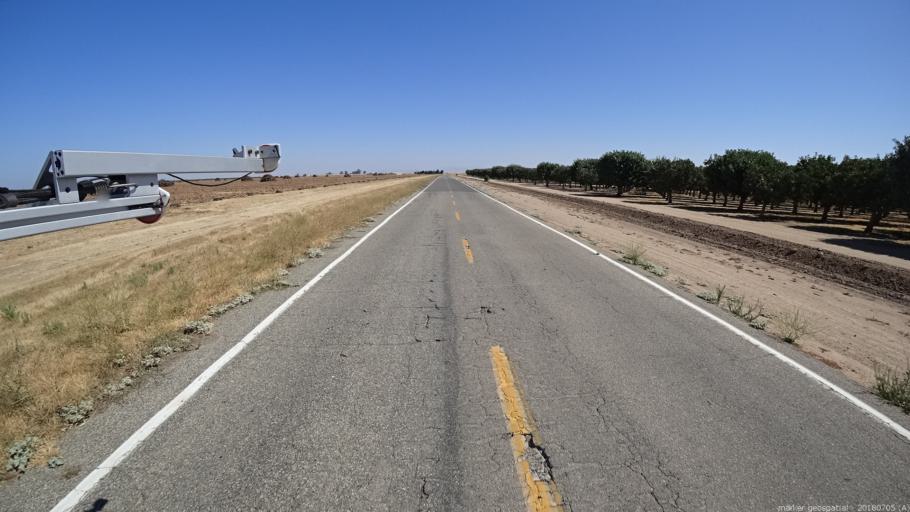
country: US
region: California
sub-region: Madera County
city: Madera Acres
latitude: 37.1091
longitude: -120.0747
